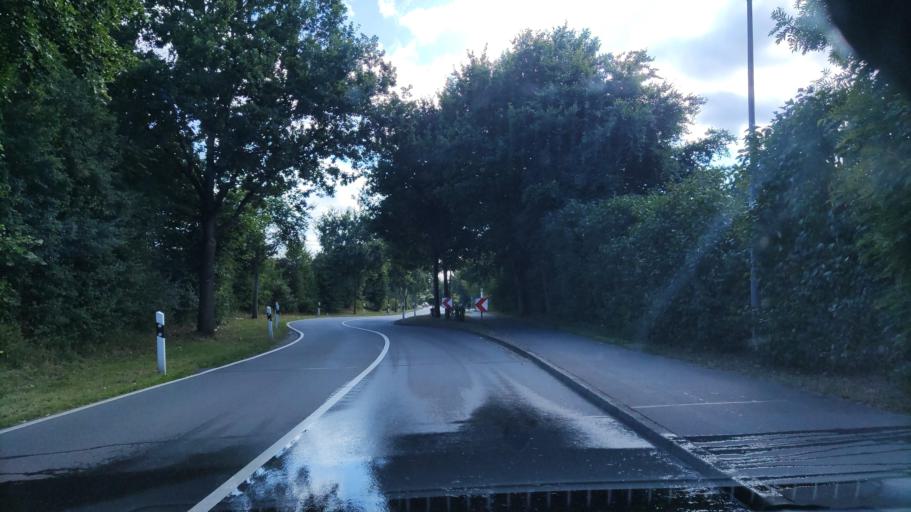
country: DE
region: Schleswig-Holstein
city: Alt Duvenstedt
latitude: 54.3555
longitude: 9.6396
